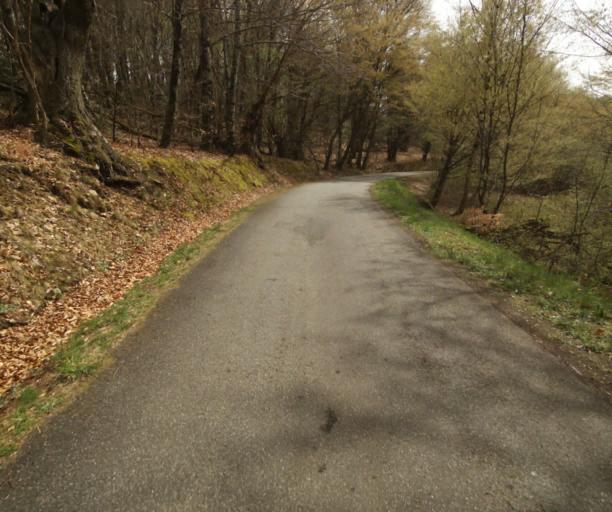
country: FR
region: Limousin
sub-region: Departement de la Correze
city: Laguenne
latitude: 45.2159
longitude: 1.8668
